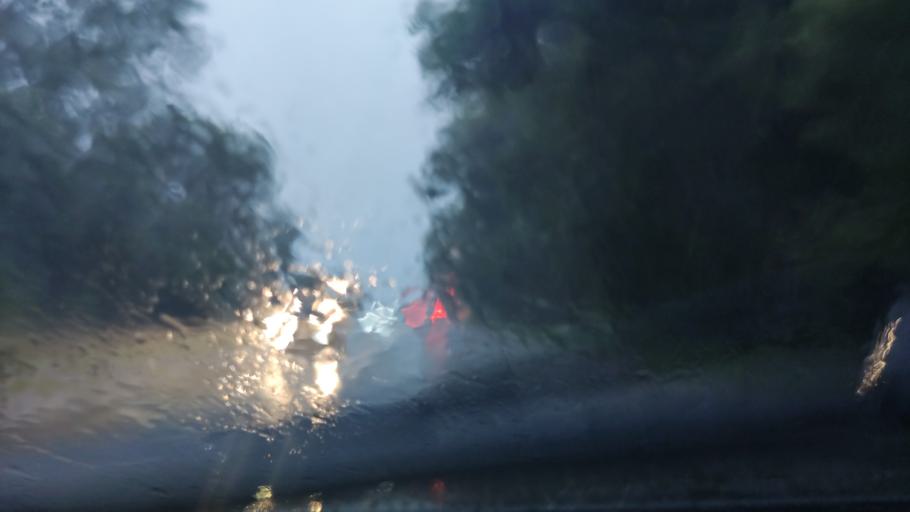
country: BR
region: Sao Paulo
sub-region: Braganca Paulista
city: Braganca Paulista
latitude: -22.7864
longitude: -46.5597
